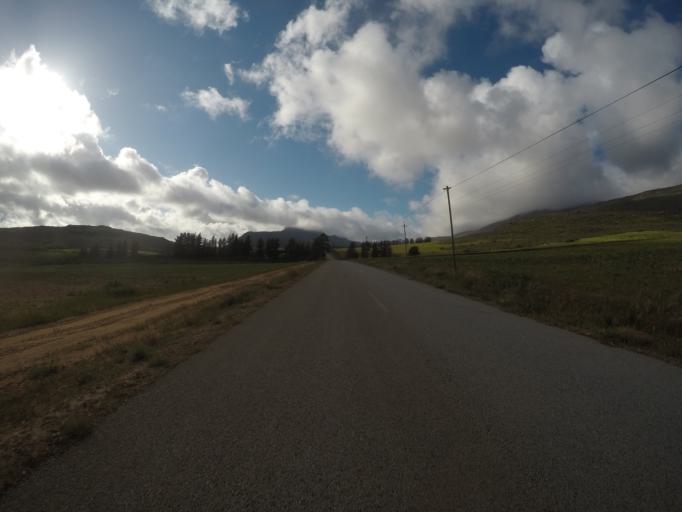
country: ZA
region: Western Cape
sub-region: West Coast District Municipality
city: Clanwilliam
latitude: -32.3456
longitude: 18.8416
